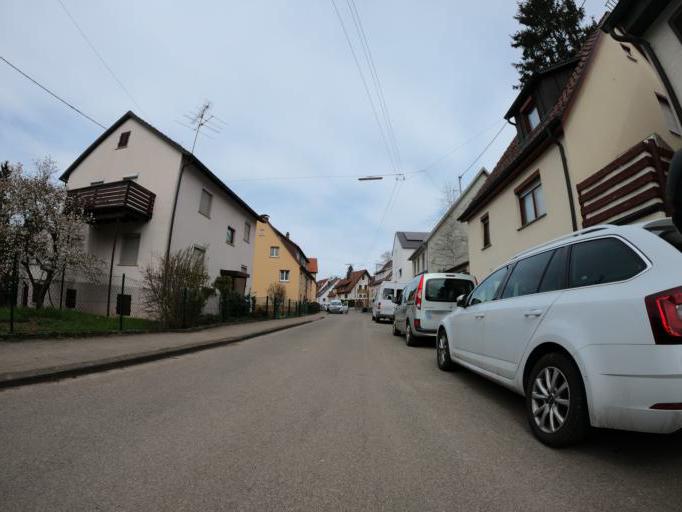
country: DE
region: Baden-Wuerttemberg
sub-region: Regierungsbezirk Stuttgart
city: Filderstadt
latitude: 48.6491
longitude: 9.2148
